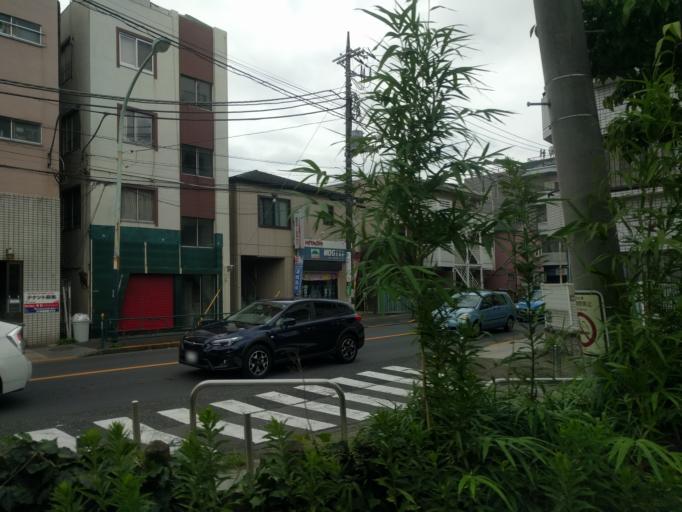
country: JP
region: Tokyo
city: Tokyo
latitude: 35.6571
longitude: 139.6438
